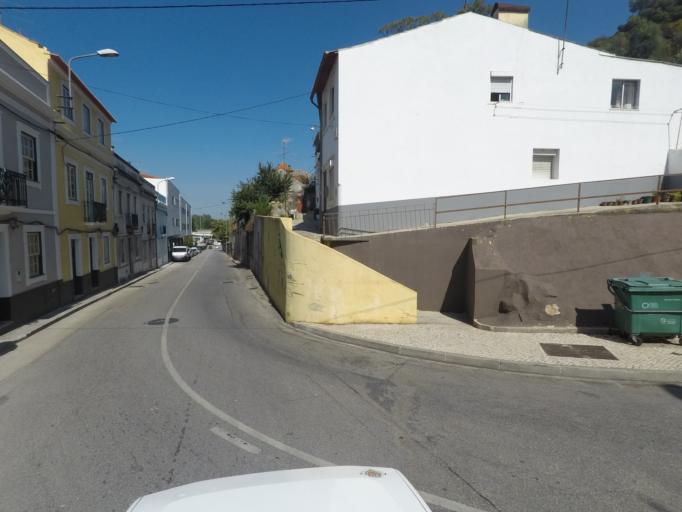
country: PT
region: Coimbra
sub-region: Coimbra
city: Coimbra
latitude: 40.2165
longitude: -8.4356
